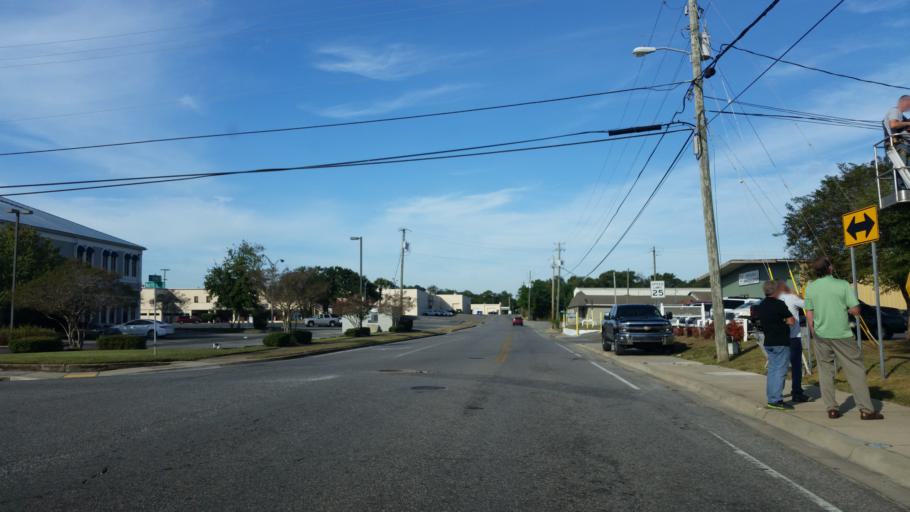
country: US
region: Florida
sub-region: Escambia County
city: Goulding
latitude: 30.4488
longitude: -87.2355
